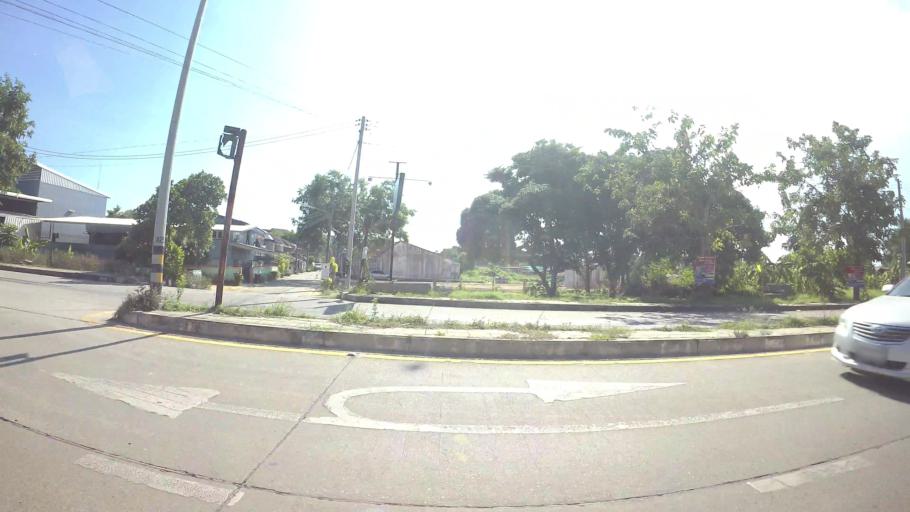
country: TH
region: Rayong
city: Rayong
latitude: 12.6730
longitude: 101.2944
